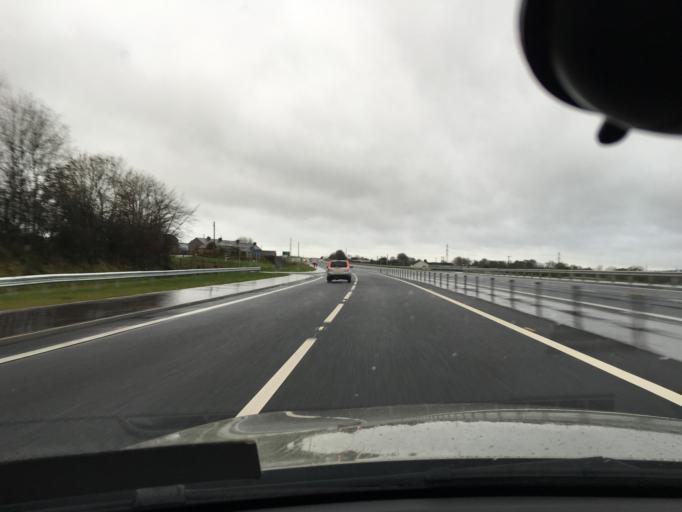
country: GB
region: Northern Ireland
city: Ballyclare
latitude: 54.7929
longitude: -5.9352
